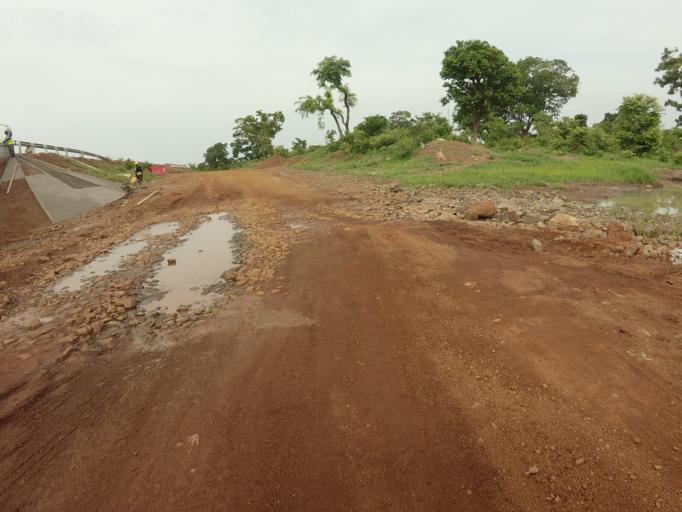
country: GH
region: Northern
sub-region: Yendi
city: Yendi
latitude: 9.7939
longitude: -0.1145
